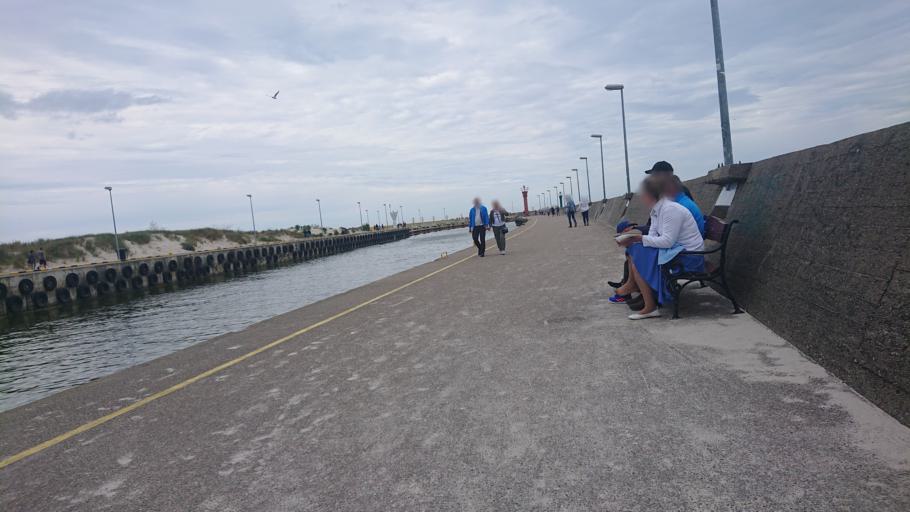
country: PL
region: Pomeranian Voivodeship
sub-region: Powiat leborski
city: Leba
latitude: 54.7674
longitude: 17.5515
